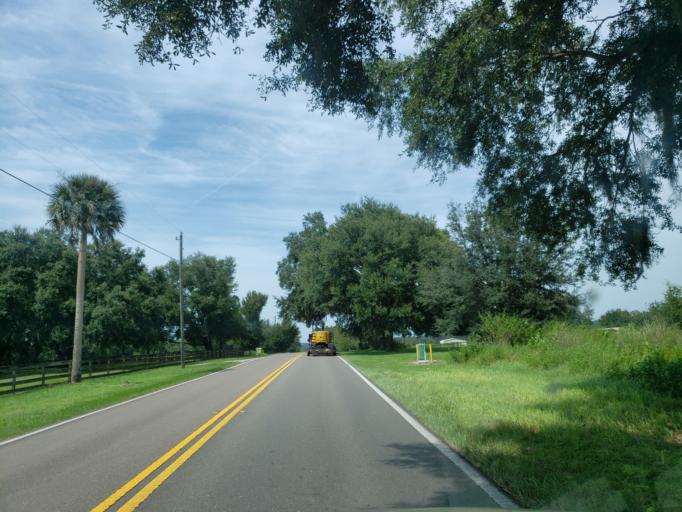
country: US
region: Florida
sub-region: Pasco County
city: San Antonio
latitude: 28.3047
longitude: -82.2787
